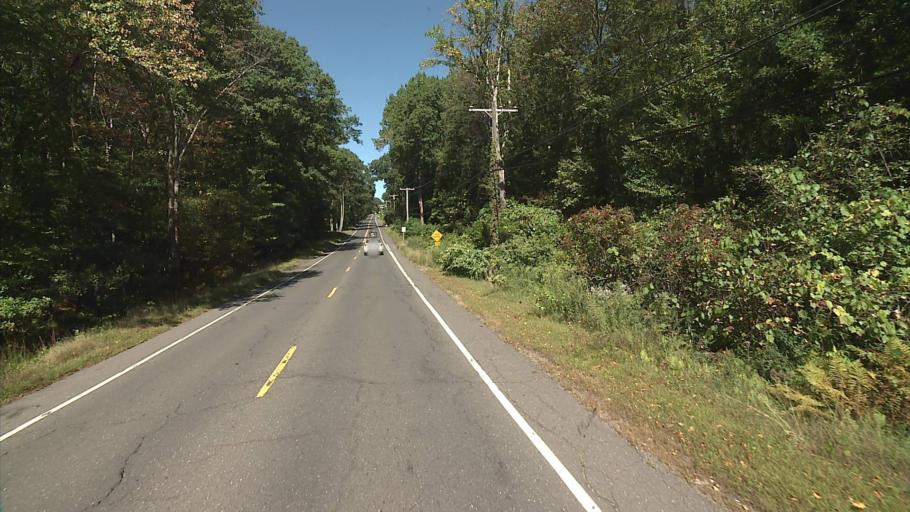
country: US
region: Connecticut
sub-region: New Haven County
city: Prospect
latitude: 41.4877
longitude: -72.9731
